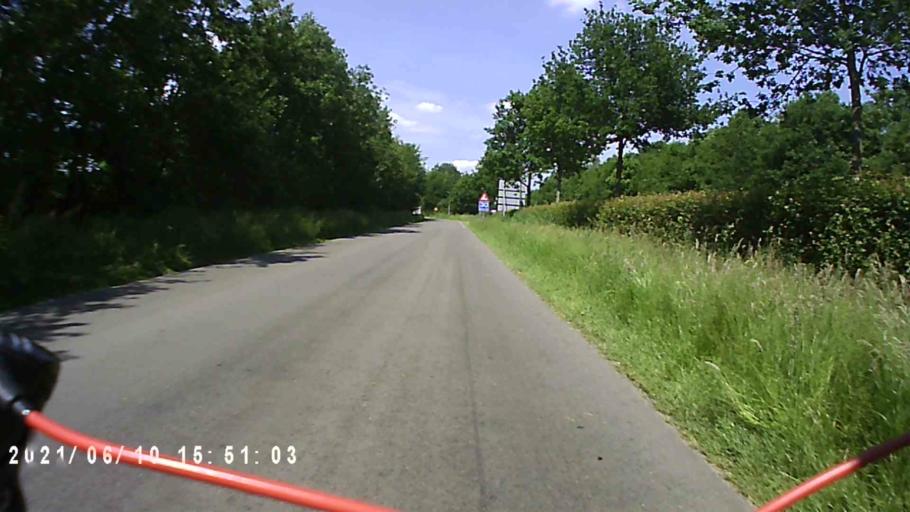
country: NL
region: Friesland
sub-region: Gemeente Achtkarspelen
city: Harkema
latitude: 53.1715
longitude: 6.1182
